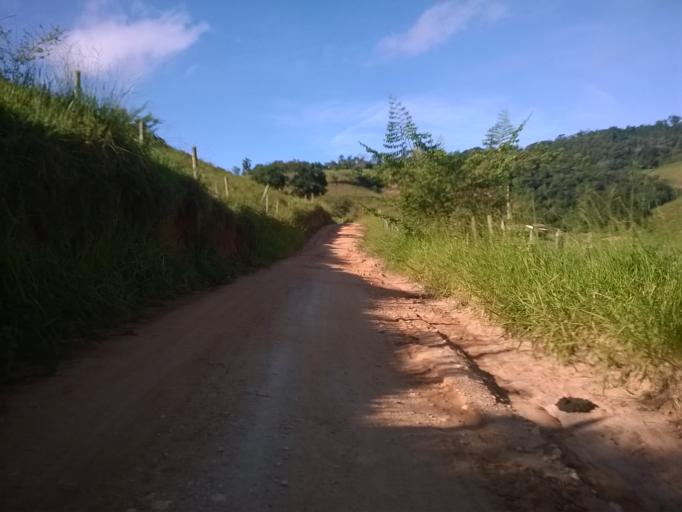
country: BR
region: Minas Gerais
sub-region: Uba
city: Uba
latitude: -21.0915
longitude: -43.0134
